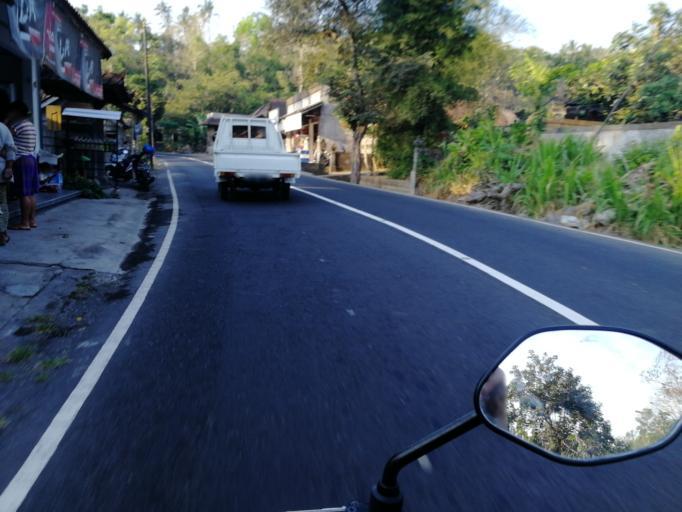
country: ID
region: Bali
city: Tistagede
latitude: -8.3756
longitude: 115.6079
